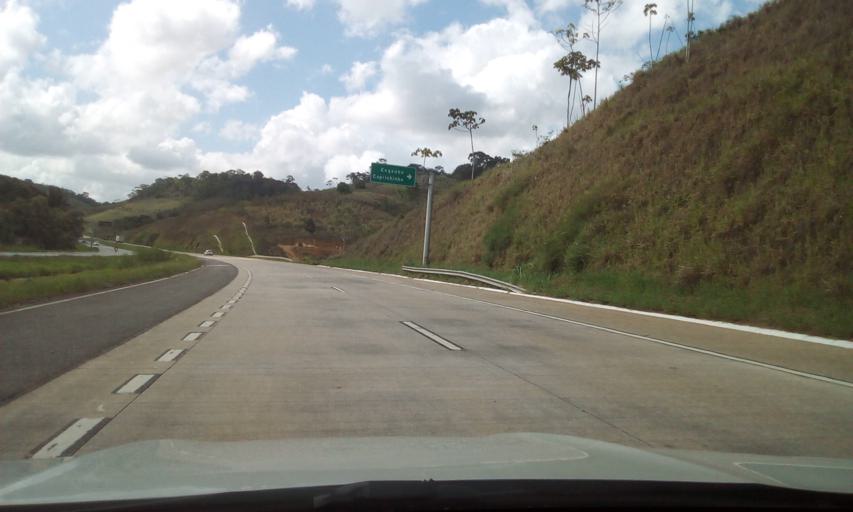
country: BR
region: Pernambuco
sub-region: Palmares
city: Palmares
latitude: -8.7355
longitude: -35.6099
